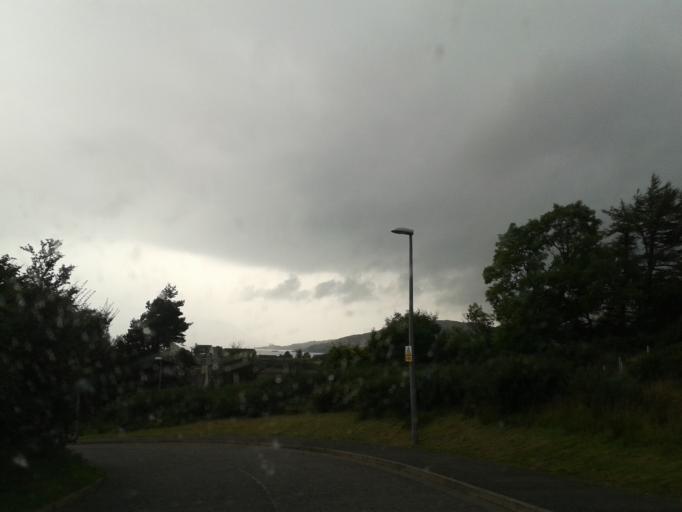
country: GB
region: Scotland
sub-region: Highland
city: Fort William
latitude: 57.2792
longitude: -5.5136
